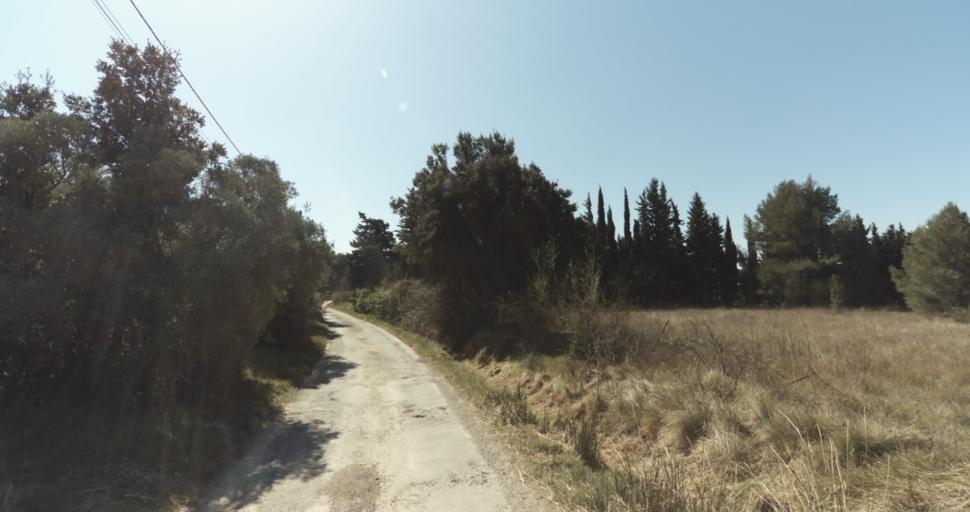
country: FR
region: Provence-Alpes-Cote d'Azur
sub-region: Departement des Bouches-du-Rhone
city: Pelissanne
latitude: 43.6150
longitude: 5.1576
